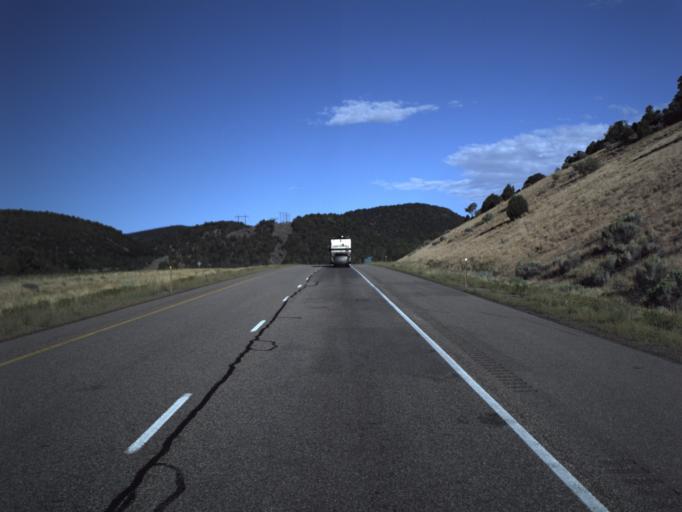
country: US
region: Utah
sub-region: Beaver County
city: Beaver
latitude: 38.5777
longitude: -112.4749
